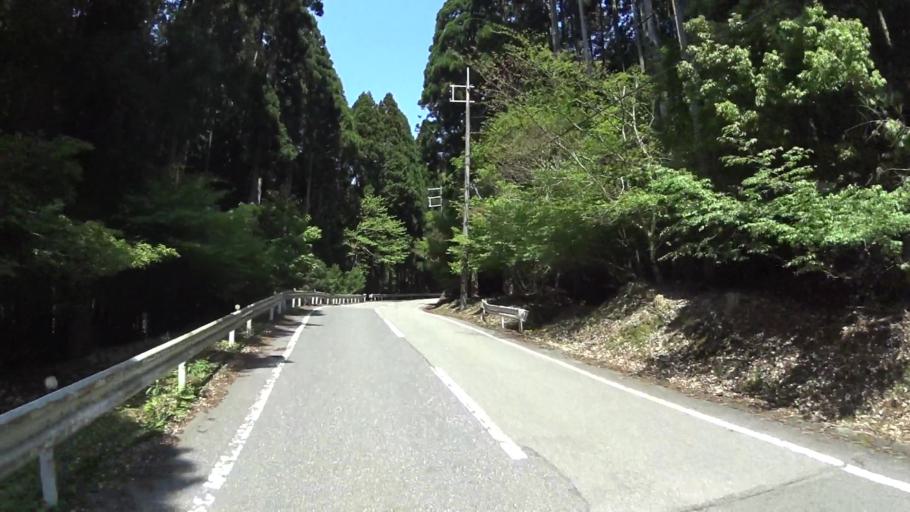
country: JP
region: Shiga Prefecture
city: Kitahama
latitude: 35.1527
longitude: 135.8146
